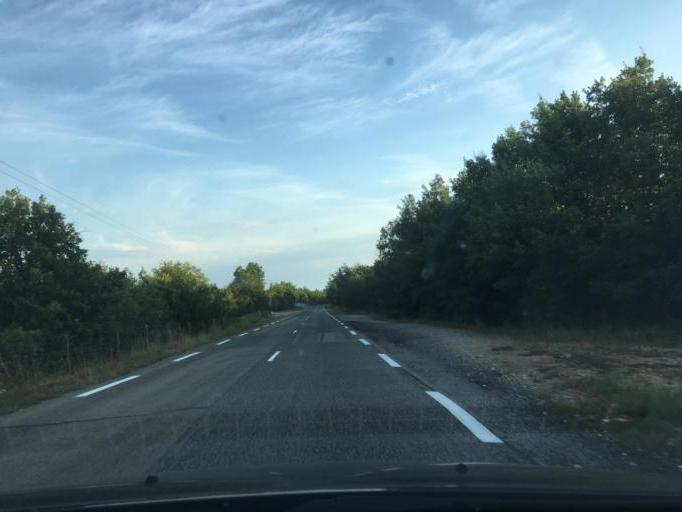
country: FR
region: Provence-Alpes-Cote d'Azur
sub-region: Departement du Var
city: Aups
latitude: 43.6947
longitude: 6.2185
